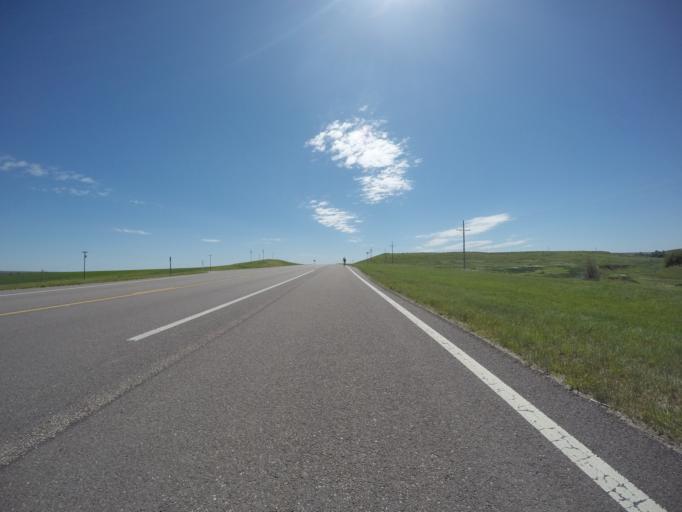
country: US
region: Kansas
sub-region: Rawlins County
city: Atwood
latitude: 39.8134
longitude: -101.0275
